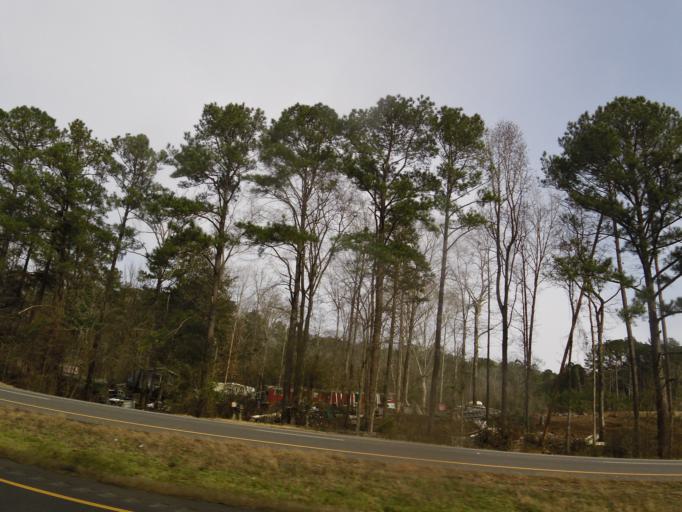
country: US
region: Alabama
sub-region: Dale County
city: Ozark
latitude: 31.5213
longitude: -85.7137
